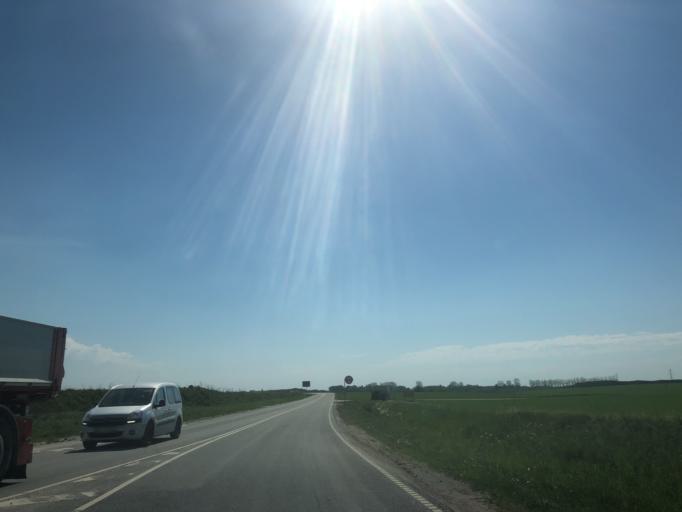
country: DK
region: Zealand
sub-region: Roskilde Kommune
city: Vindinge
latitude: 55.6275
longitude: 12.1239
